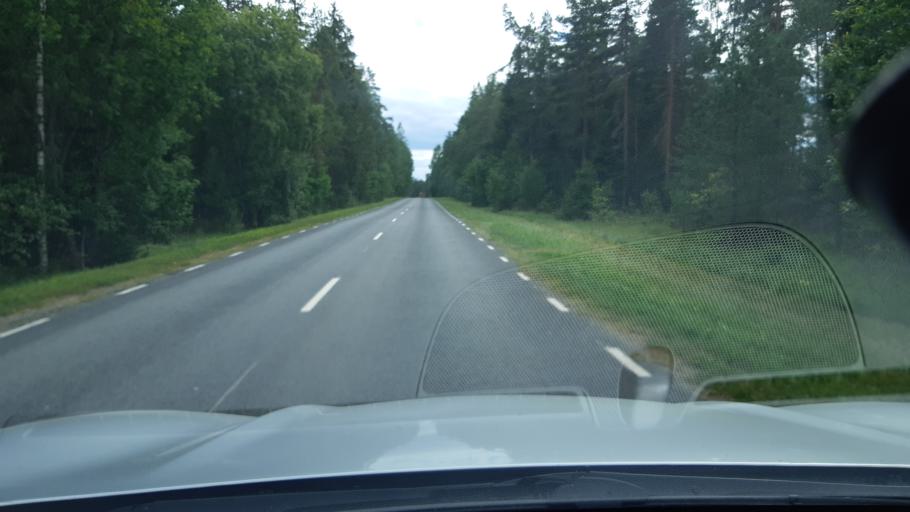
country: EE
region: Raplamaa
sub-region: Maerjamaa vald
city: Marjamaa
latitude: 59.0331
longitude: 24.5525
